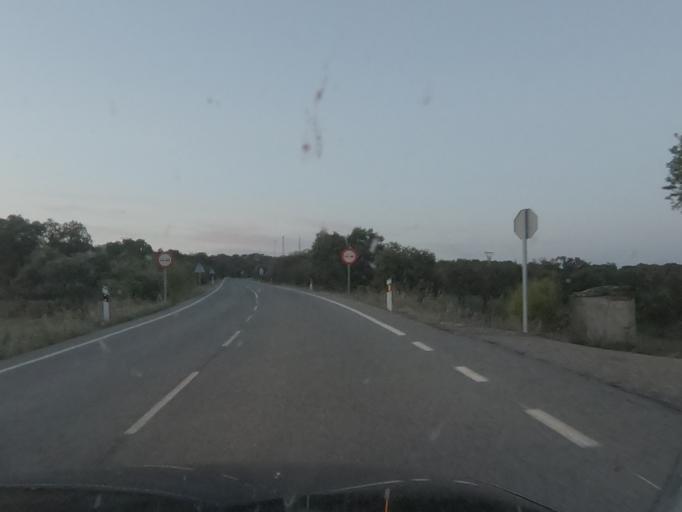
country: ES
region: Extremadura
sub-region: Provincia de Caceres
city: Alcantara
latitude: 39.7390
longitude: -6.9030
